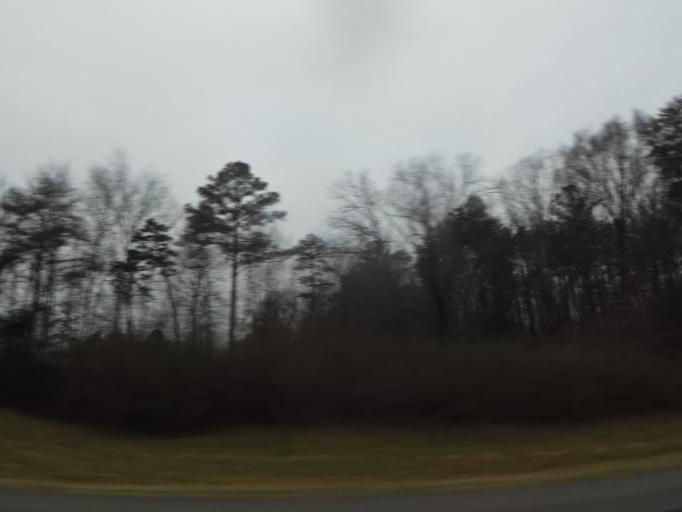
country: US
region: Alabama
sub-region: Cullman County
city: Good Hope
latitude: 34.0473
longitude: -86.8670
